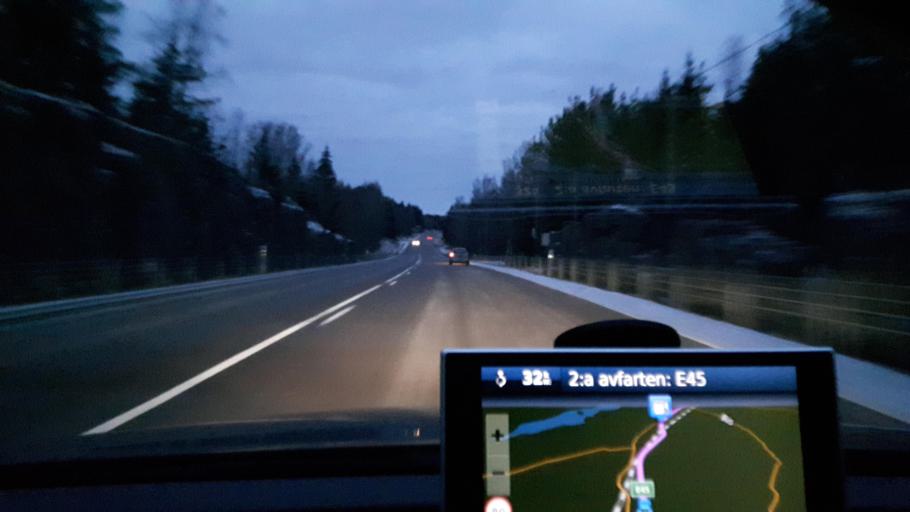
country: SE
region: Vaestra Goetaland
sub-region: Vanersborgs Kommun
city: Vanersborg
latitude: 58.4455
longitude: 12.2806
